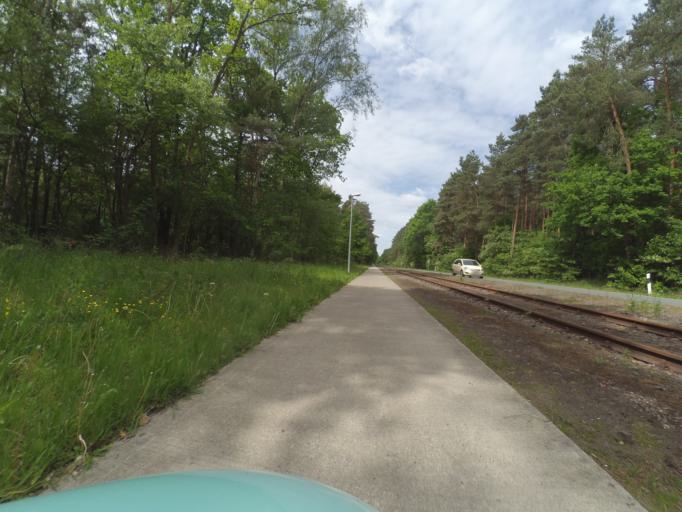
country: DE
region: Lower Saxony
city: Neustadt am Rubenberge
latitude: 52.4672
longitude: 9.4418
